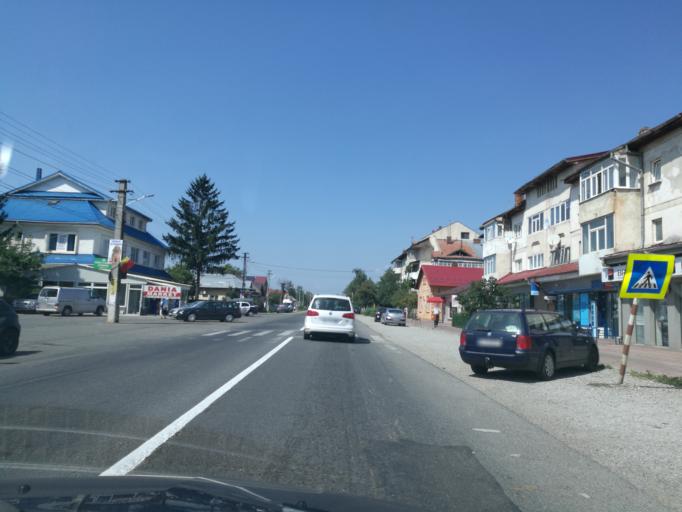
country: RO
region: Neamt
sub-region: Comuna Roznov
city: Roznov
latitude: 46.8384
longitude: 26.5065
